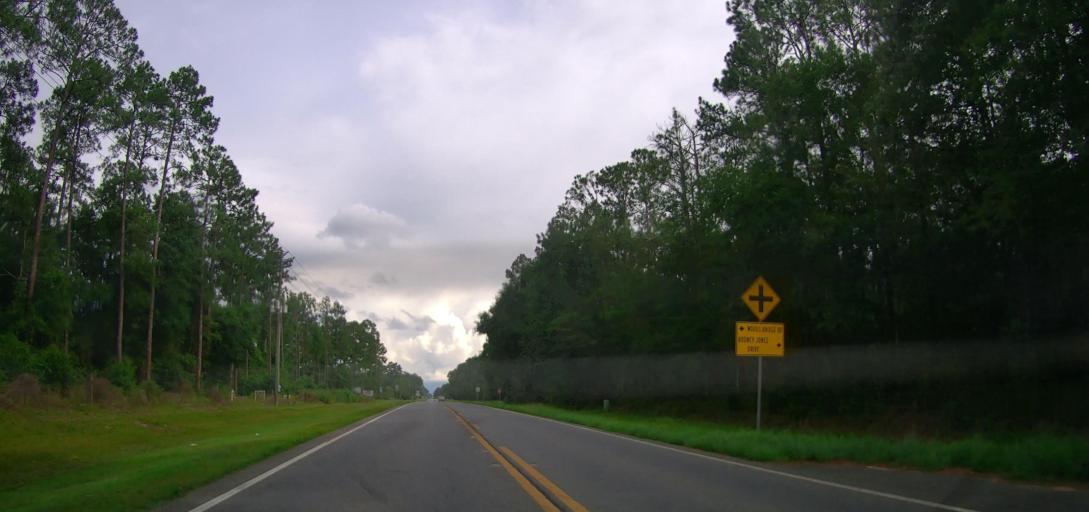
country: US
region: Georgia
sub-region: Wayne County
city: Jesup
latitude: 31.6654
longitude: -81.9165
